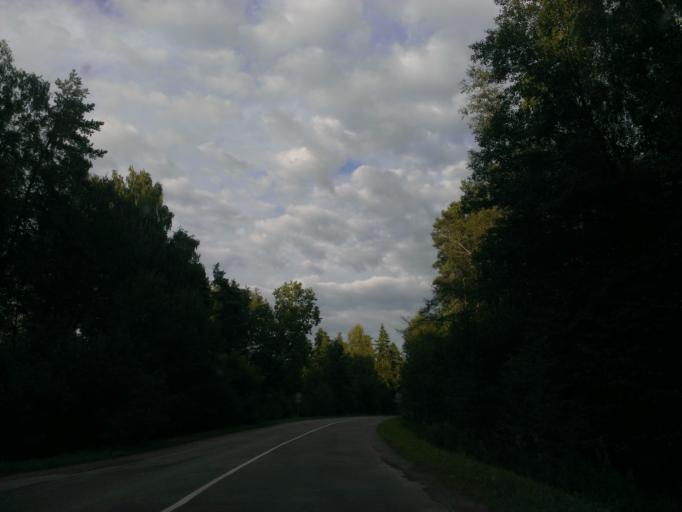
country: LV
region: Ikskile
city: Ikskile
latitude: 56.8526
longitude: 24.5054
